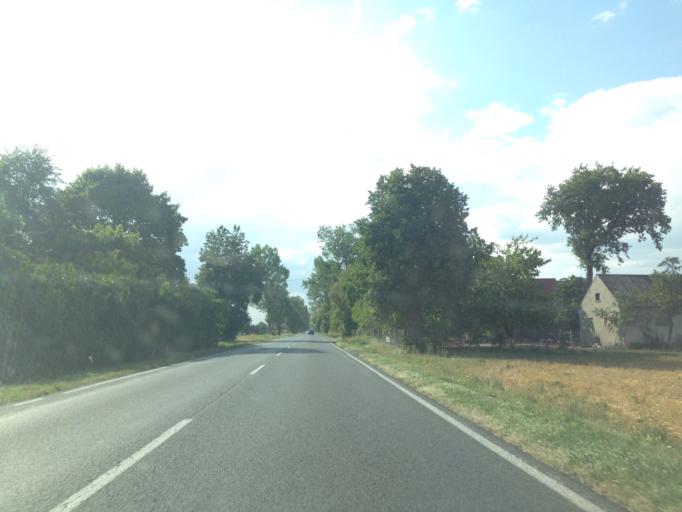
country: PL
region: Kujawsko-Pomorskie
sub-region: Powiat swiecki
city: Bukowiec
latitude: 53.4500
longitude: 18.2381
